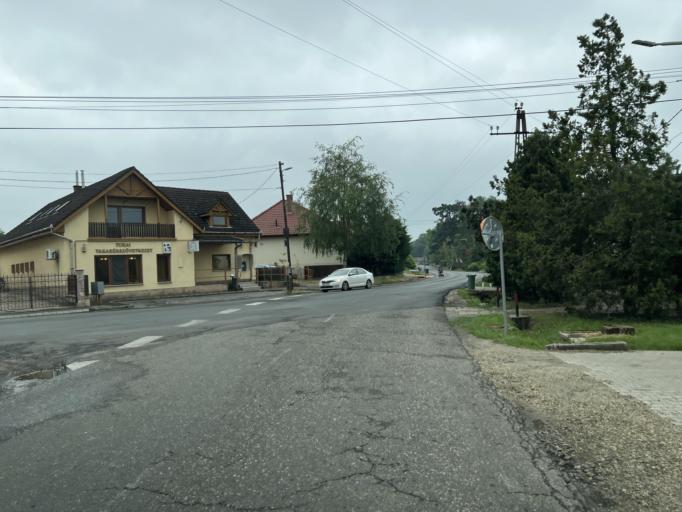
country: HU
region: Pest
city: Zsambok
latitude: 47.5460
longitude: 19.6041
